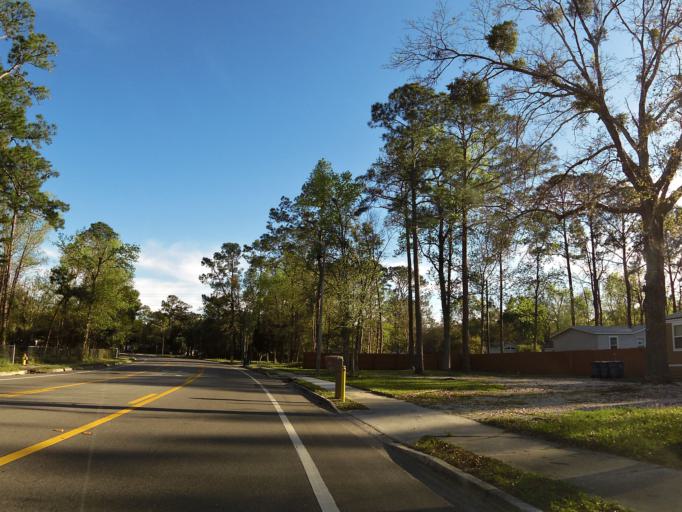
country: US
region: Florida
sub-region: Duval County
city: Jacksonville
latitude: 30.4633
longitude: -81.6178
